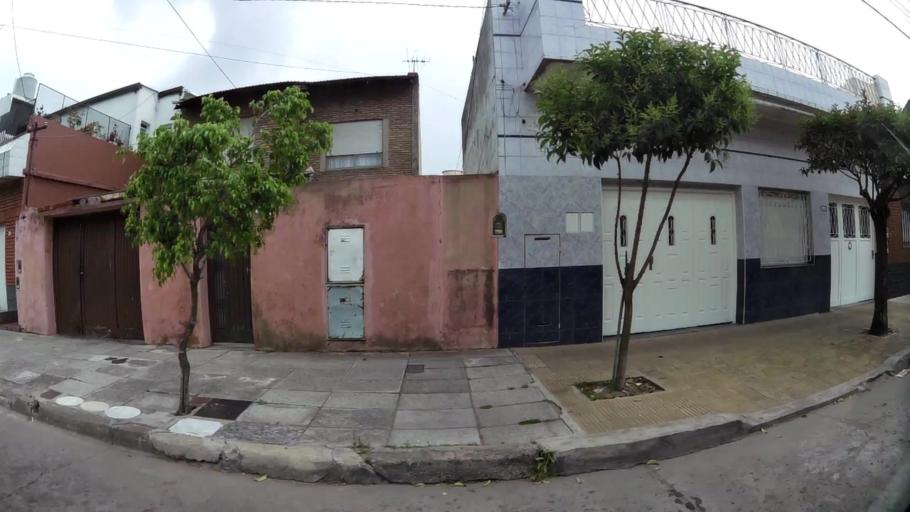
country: AR
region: Buenos Aires
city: San Justo
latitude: -34.6898
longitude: -58.5299
